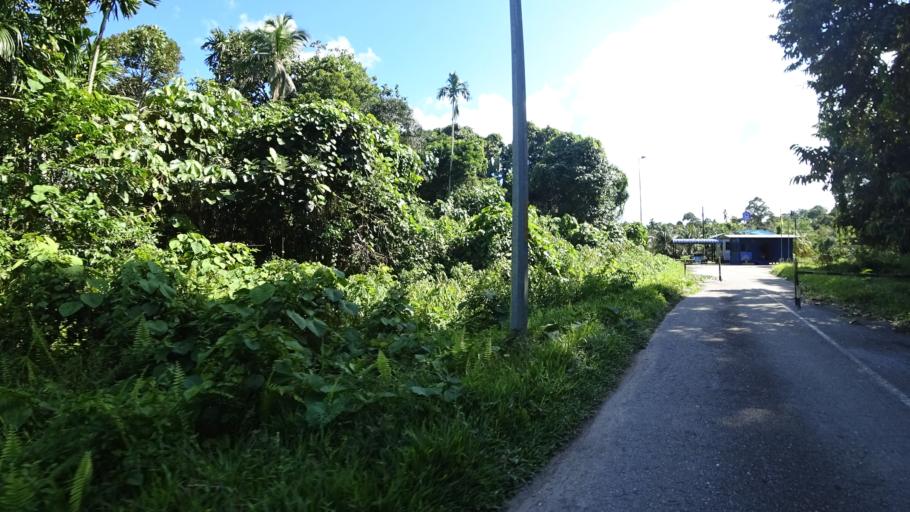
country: BN
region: Tutong
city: Tutong
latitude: 4.7344
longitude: 114.7904
